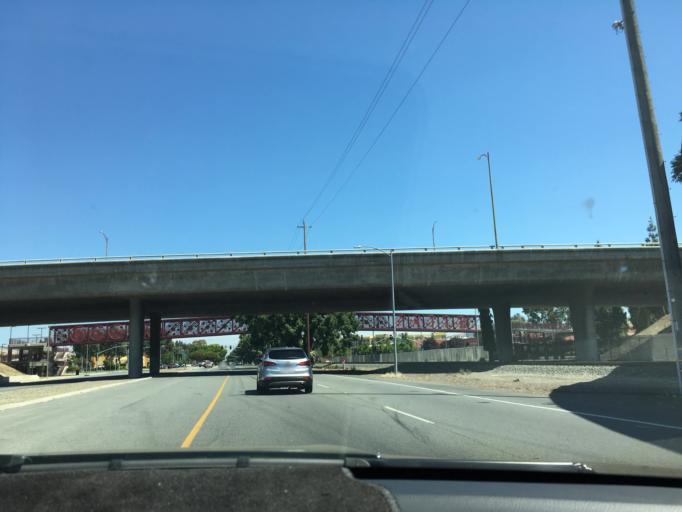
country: US
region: California
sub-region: Santa Clara County
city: Seven Trees
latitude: 37.2561
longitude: -121.8033
